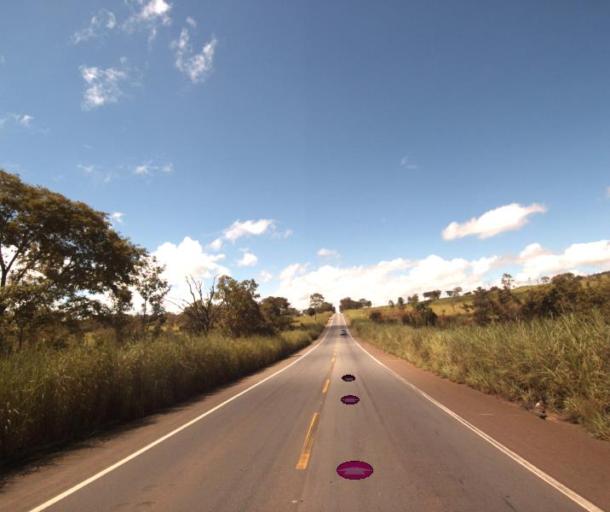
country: BR
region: Goias
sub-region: Jaragua
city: Jaragua
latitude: -15.8094
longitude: -49.2944
